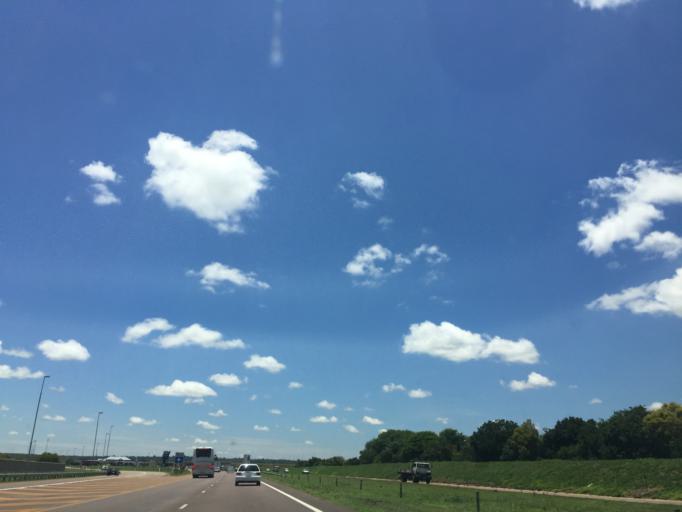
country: ZA
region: Gauteng
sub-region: City of Tshwane Metropolitan Municipality
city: Pretoria
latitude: -25.6426
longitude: 28.2368
